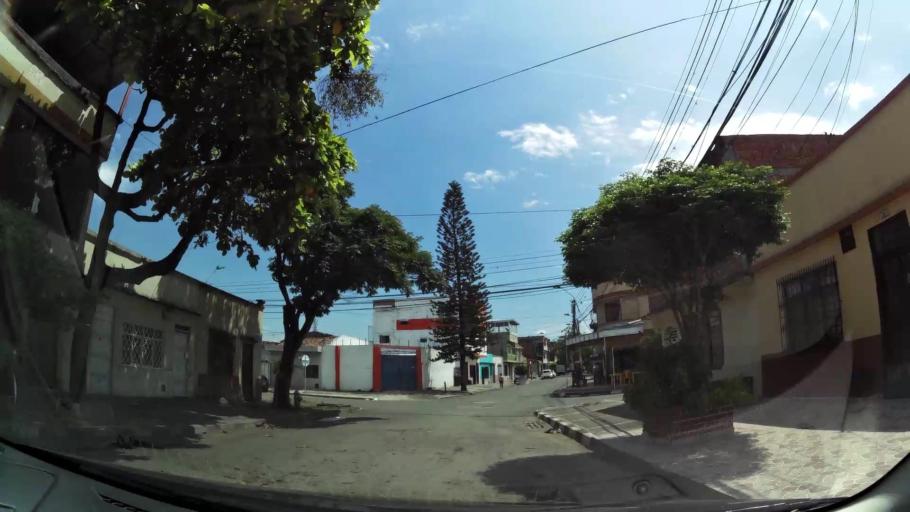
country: CO
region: Valle del Cauca
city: Cali
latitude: 3.4438
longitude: -76.5153
